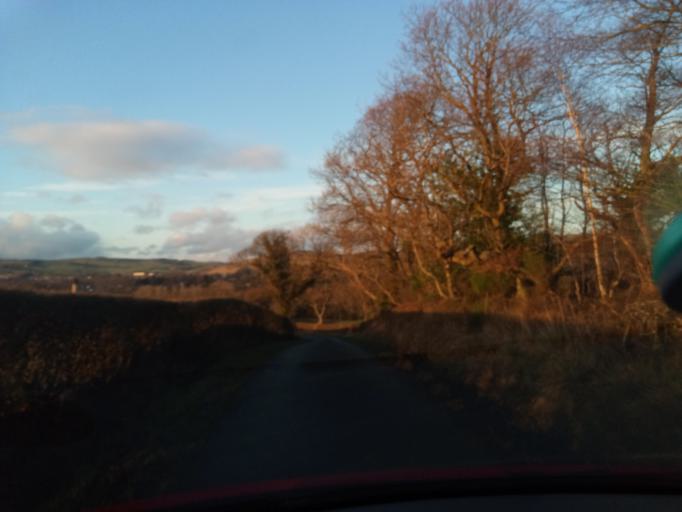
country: GB
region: Scotland
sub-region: The Scottish Borders
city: Melrose
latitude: 55.5926
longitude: -2.7367
